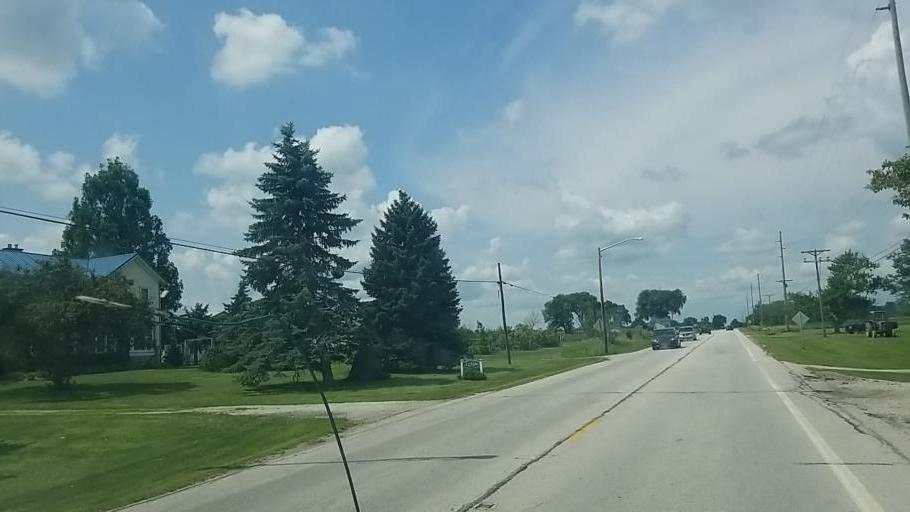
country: US
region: Ohio
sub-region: Wayne County
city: West Salem
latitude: 41.0273
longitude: -82.1284
